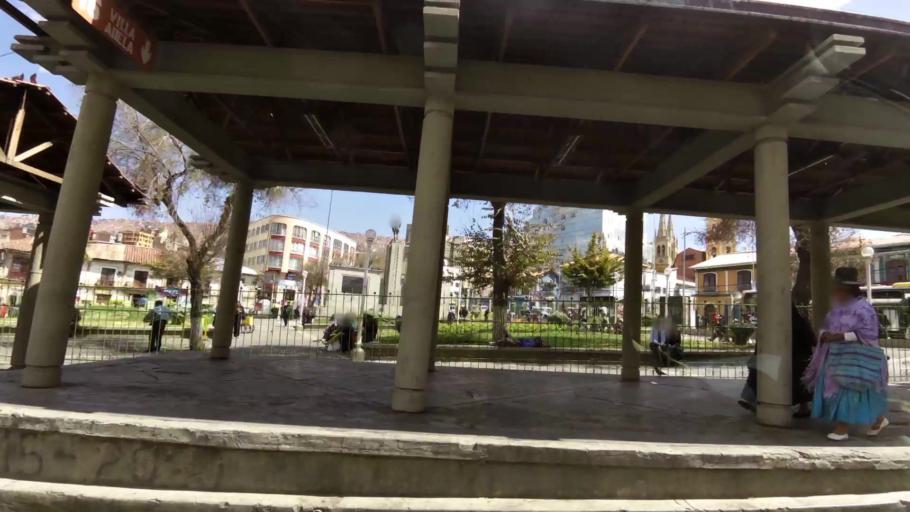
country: BO
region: La Paz
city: La Paz
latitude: -16.4931
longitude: -68.1382
